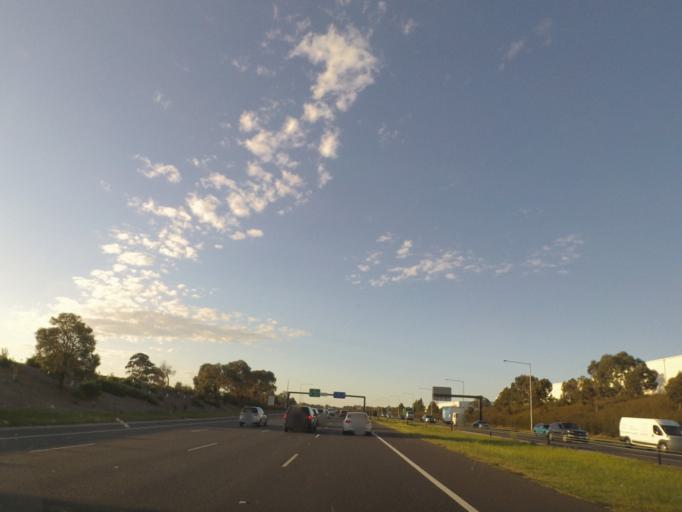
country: AU
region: Victoria
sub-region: Monash
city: Mulgrave
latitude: -37.9095
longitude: 145.2159
